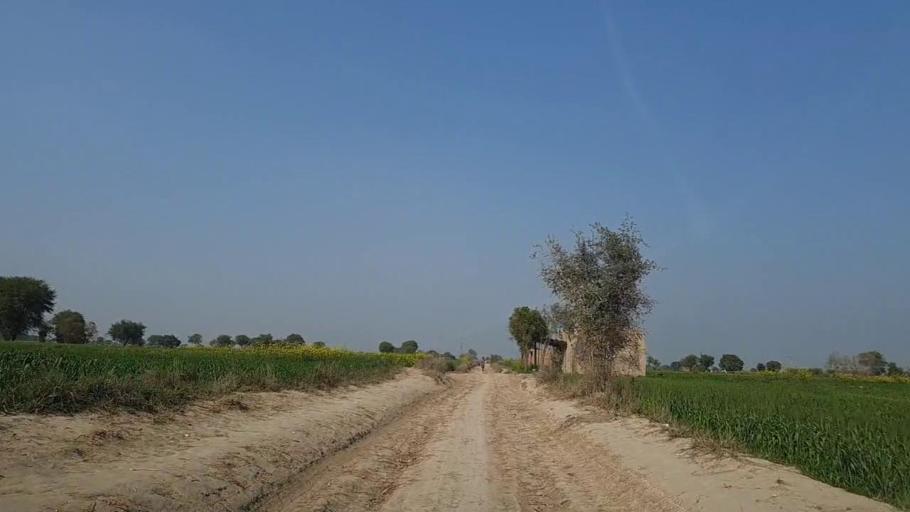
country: PK
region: Sindh
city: Moro
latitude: 26.6817
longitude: 67.9274
